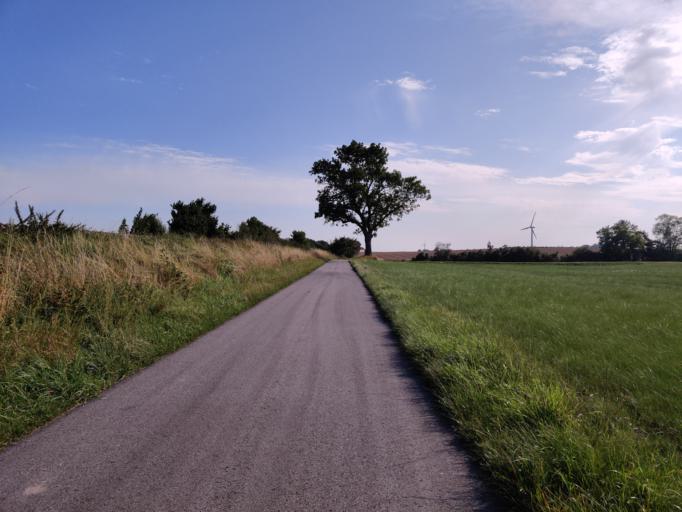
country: DK
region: Zealand
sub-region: Guldborgsund Kommune
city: Nykobing Falster
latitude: 54.6857
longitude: 11.9005
